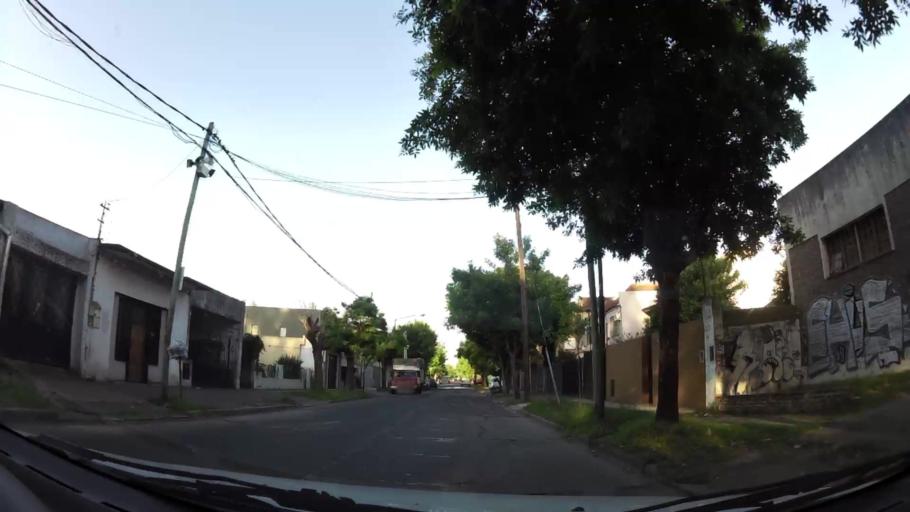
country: AR
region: Buenos Aires
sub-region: Partido de San Isidro
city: San Isidro
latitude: -34.4710
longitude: -58.5532
